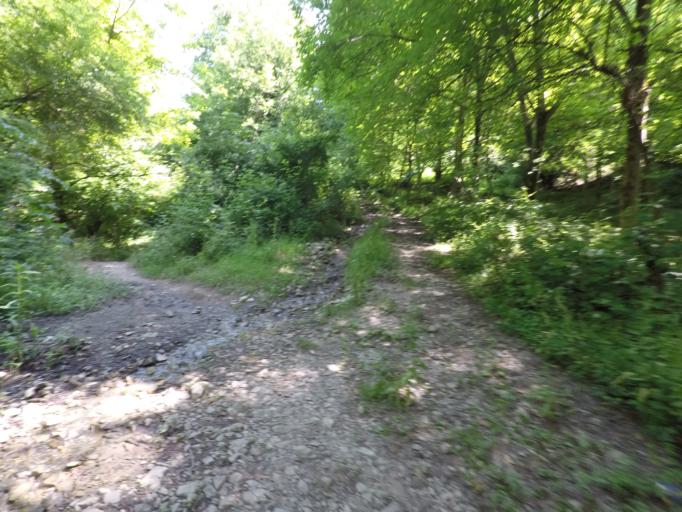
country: AZ
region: Qakh Rayon
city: Cinarli
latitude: 41.4909
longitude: 46.8582
